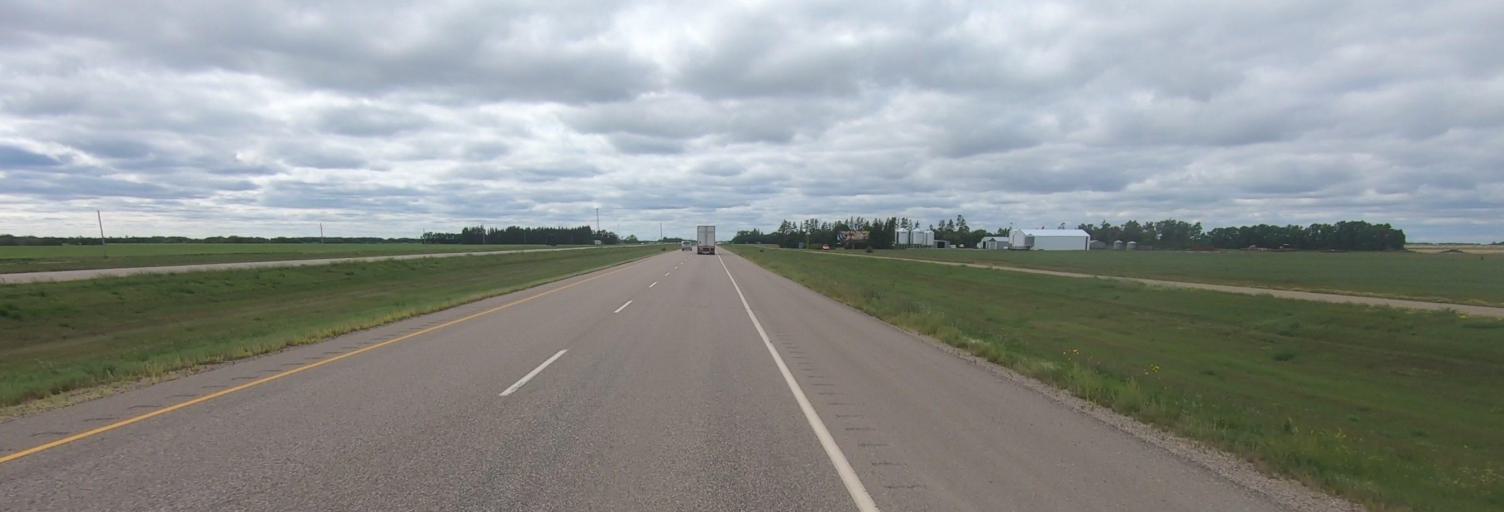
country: CA
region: Manitoba
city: Carberry
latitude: 49.9015
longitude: -99.3171
